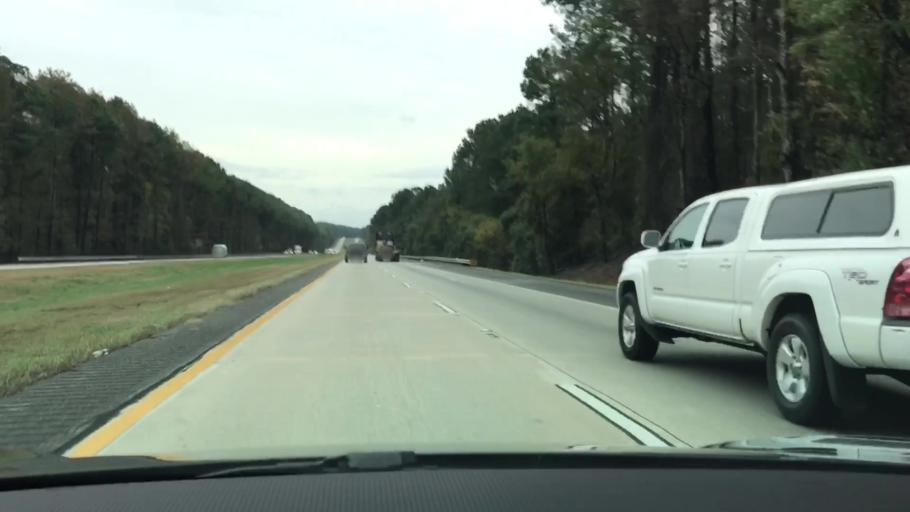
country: US
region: Georgia
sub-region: Greene County
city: Greensboro
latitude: 33.5482
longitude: -83.1572
